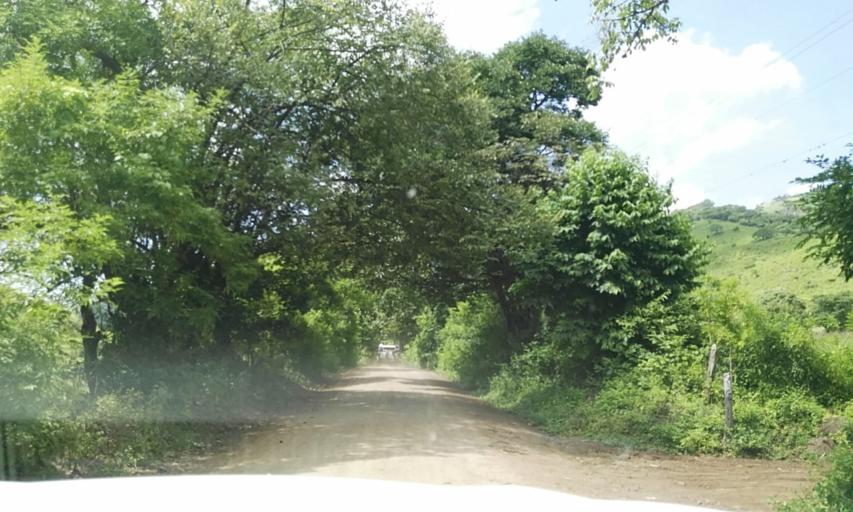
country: NI
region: Matagalpa
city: Terrabona
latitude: 12.7207
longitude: -85.9647
